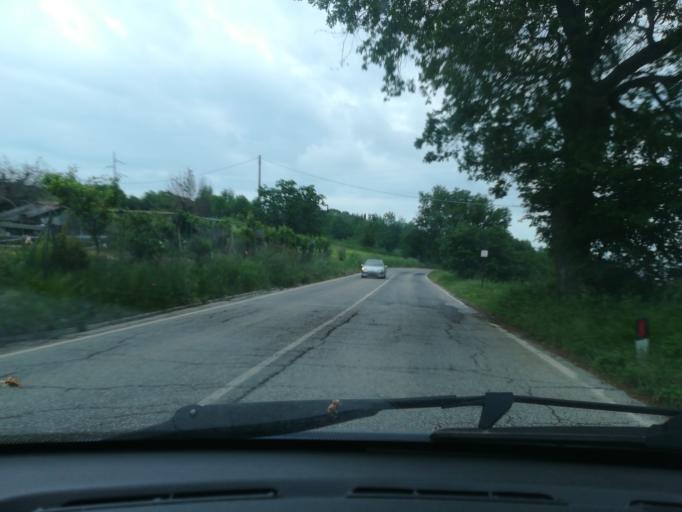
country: IT
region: The Marches
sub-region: Provincia di Macerata
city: Sforzacosta
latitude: 43.2895
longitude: 13.4134
